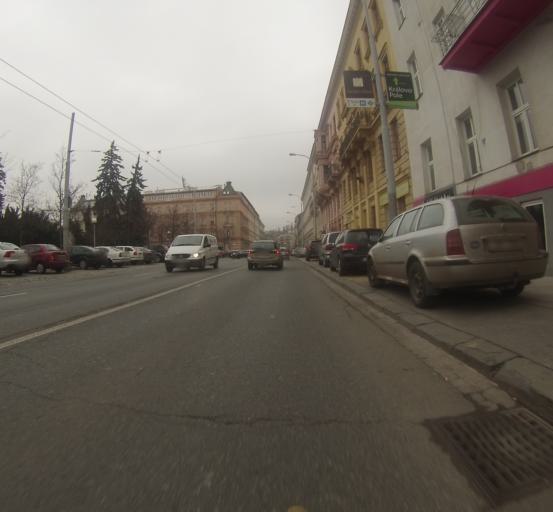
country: CZ
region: South Moravian
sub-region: Mesto Brno
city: Brno
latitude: 49.2032
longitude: 16.6136
